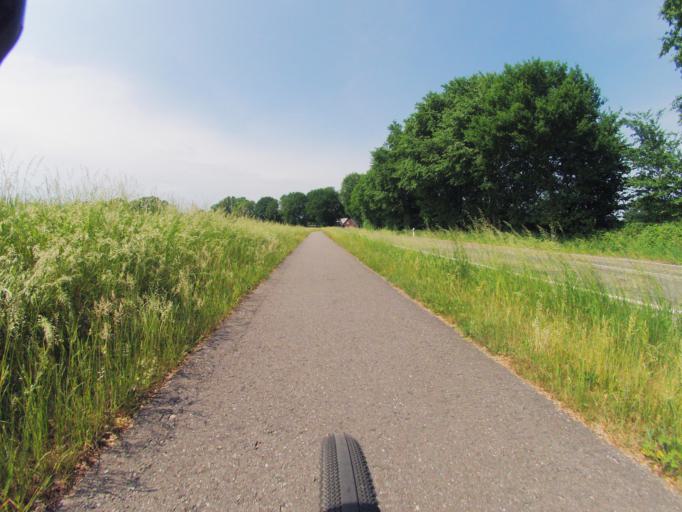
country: DE
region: North Rhine-Westphalia
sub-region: Regierungsbezirk Munster
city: Horstel
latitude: 52.3199
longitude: 7.6287
